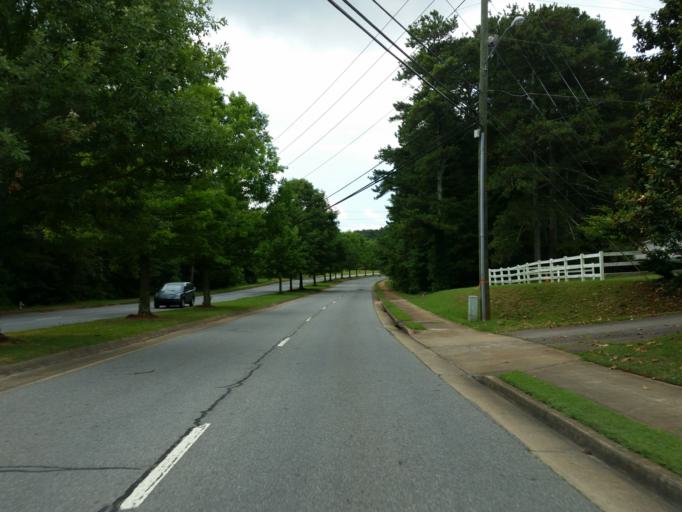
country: US
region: Georgia
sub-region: Cobb County
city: Kennesaw
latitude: 34.0760
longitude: -84.5883
